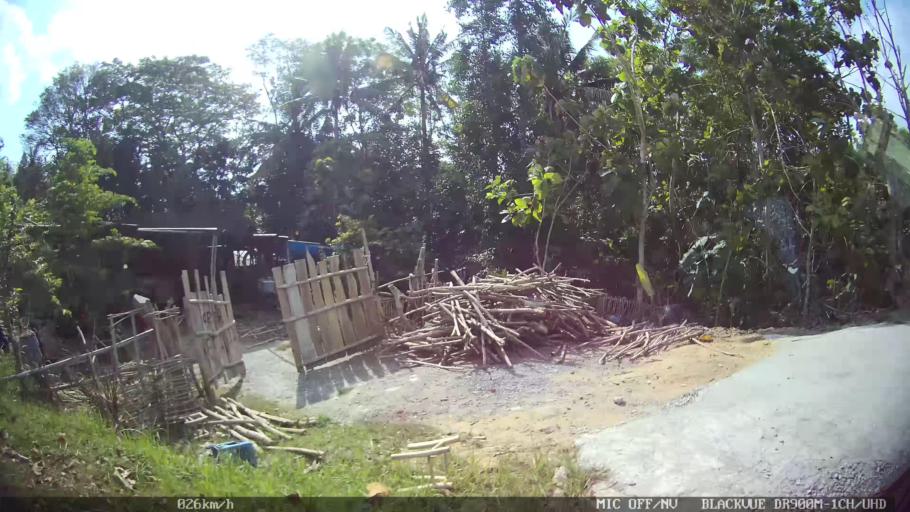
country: ID
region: Daerah Istimewa Yogyakarta
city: Kasihan
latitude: -7.8492
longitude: 110.3002
